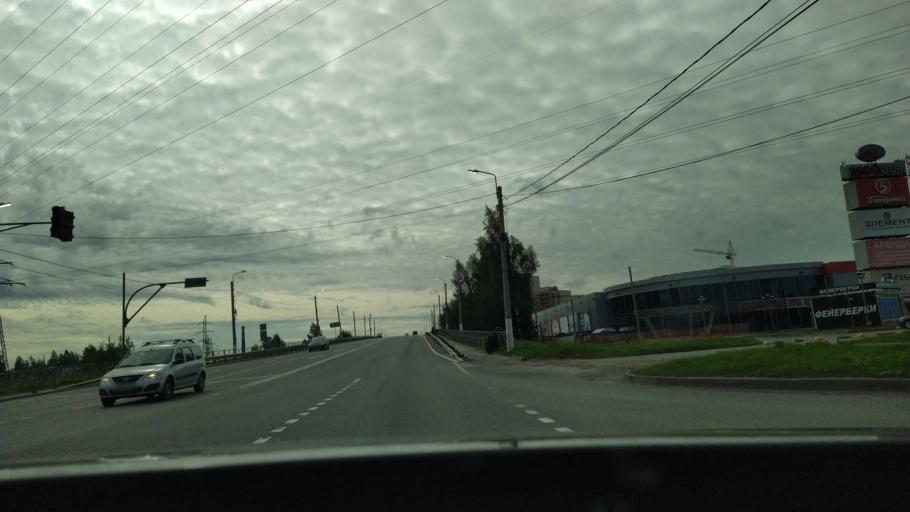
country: RU
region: Leningrad
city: Tosno
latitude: 59.5535
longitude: 30.8533
